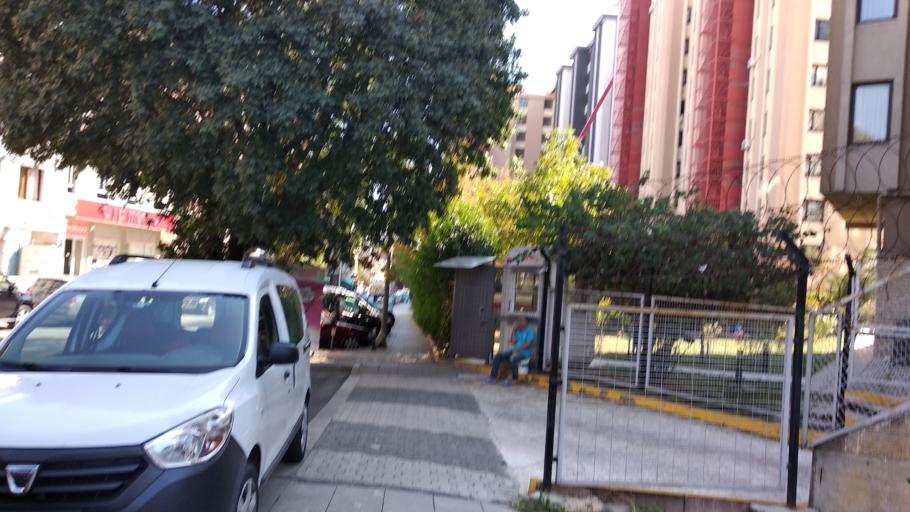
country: TR
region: Istanbul
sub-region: Atasehir
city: Atasehir
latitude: 41.0024
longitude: 29.0755
